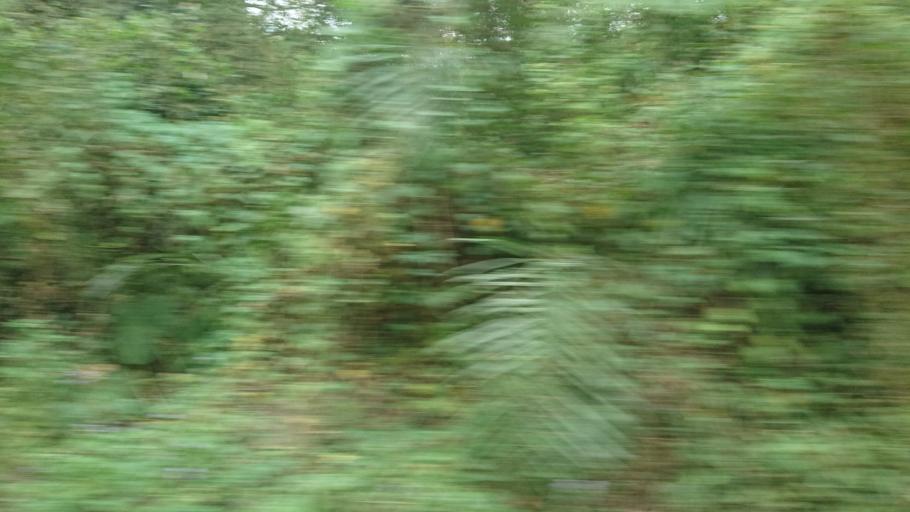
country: TW
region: Taiwan
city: Lugu
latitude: 23.5973
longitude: 120.7009
